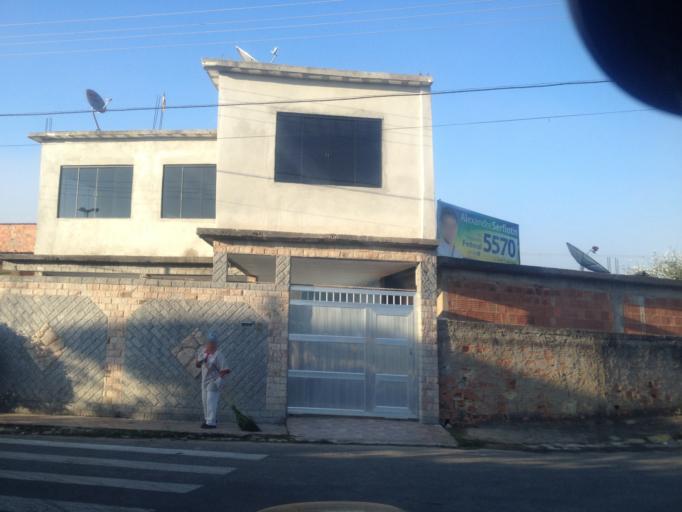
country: BR
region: Rio de Janeiro
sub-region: Porto Real
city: Porto Real
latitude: -22.4150
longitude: -44.3074
